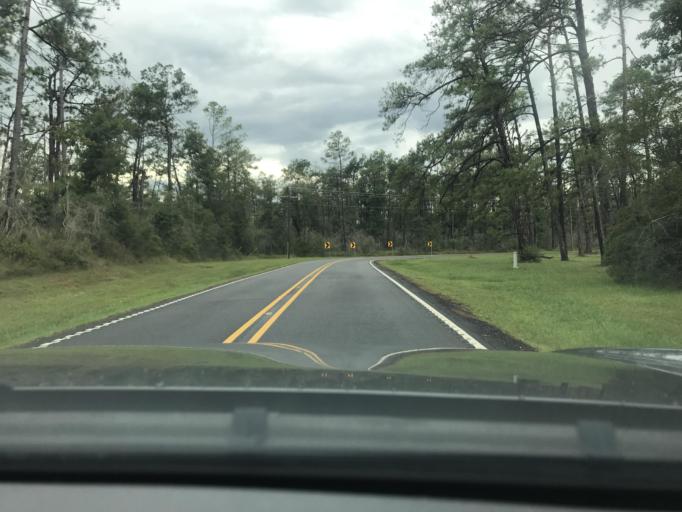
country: US
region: Louisiana
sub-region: Calcasieu Parish
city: Westlake
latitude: 30.3014
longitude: -93.2576
